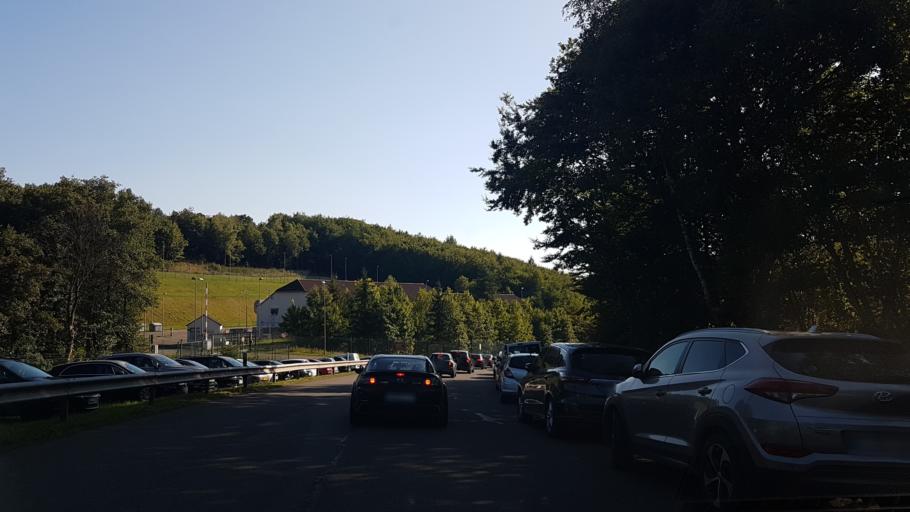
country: DE
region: Rheinland-Pfalz
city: Baumholder
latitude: 49.6267
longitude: 7.3146
